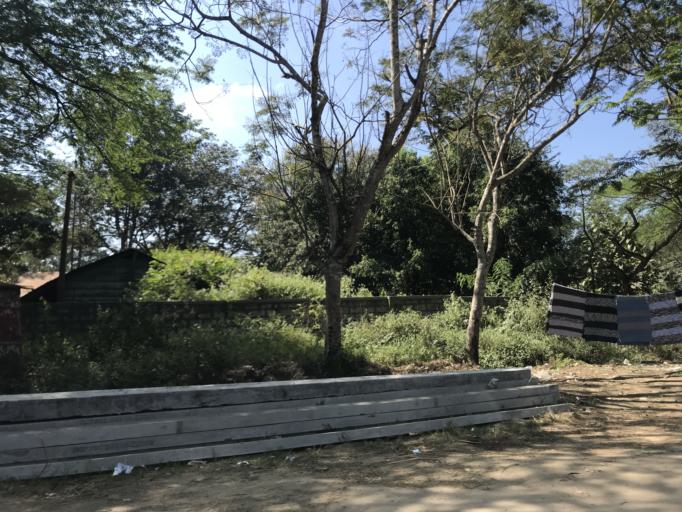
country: IN
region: Karnataka
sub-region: Mysore
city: Heggadadevankote
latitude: 12.0678
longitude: 76.3546
